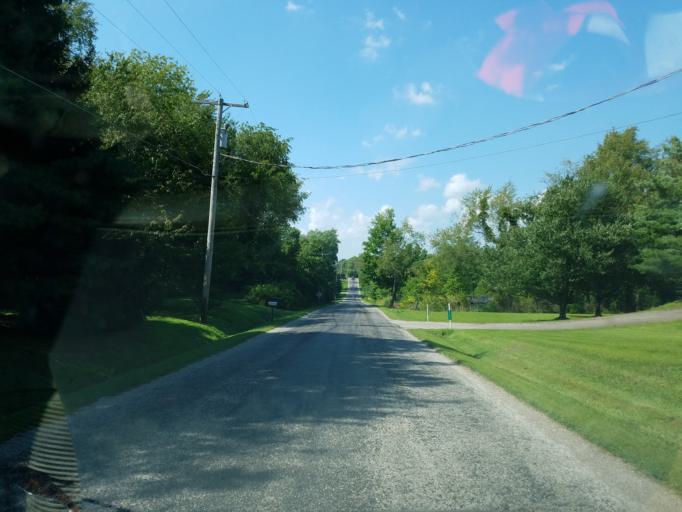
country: US
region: Ohio
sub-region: Ashland County
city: Ashland
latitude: 40.8888
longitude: -82.3490
